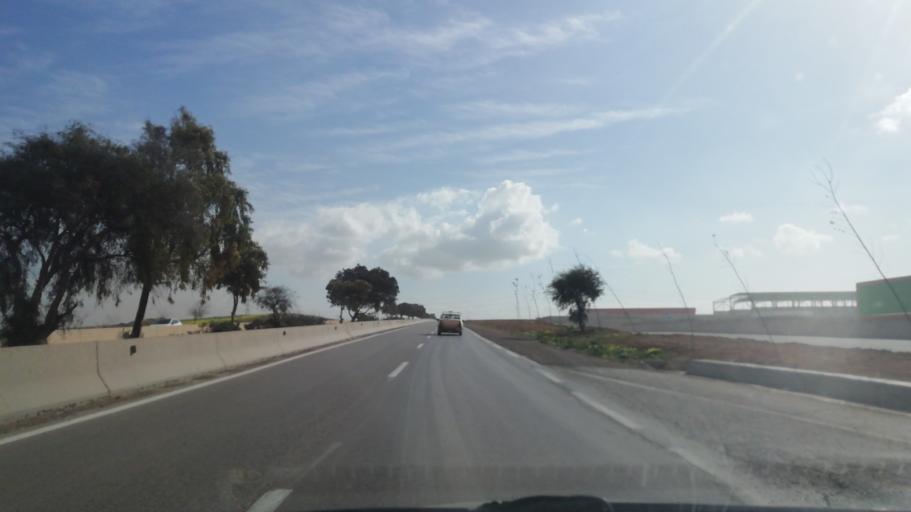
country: DZ
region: Oran
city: Ain el Bya
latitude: 35.7746
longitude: -0.2528
